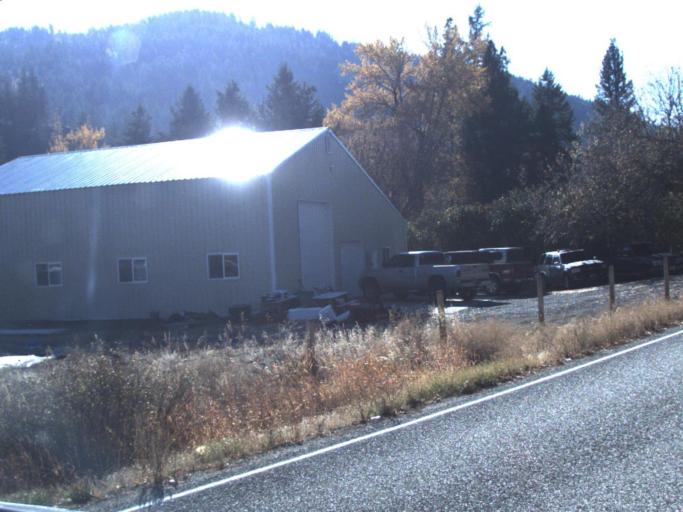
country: CA
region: British Columbia
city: Grand Forks
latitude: 48.9423
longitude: -118.5564
